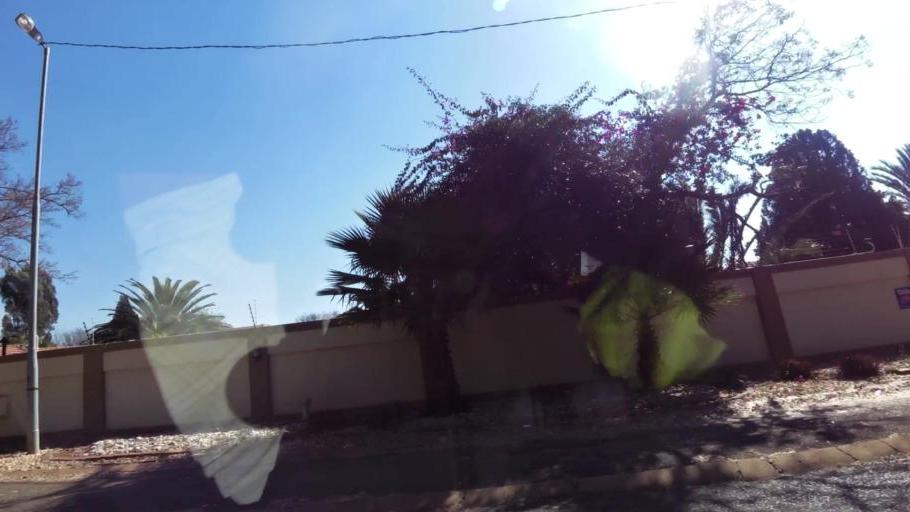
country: ZA
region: Gauteng
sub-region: City of Johannesburg Metropolitan Municipality
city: Roodepoort
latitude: -26.1346
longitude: 27.9561
